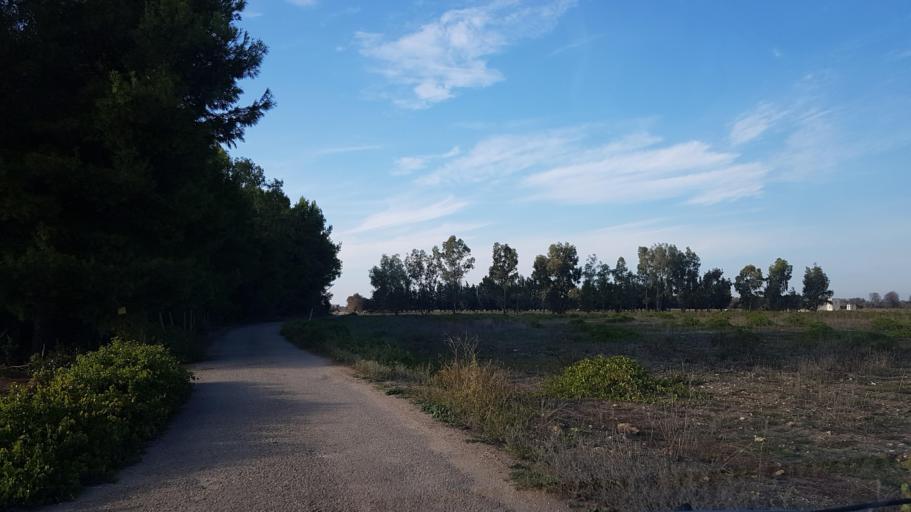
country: IT
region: Apulia
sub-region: Provincia di Brindisi
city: San Pancrazio Salentino
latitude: 40.4914
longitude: 17.8553
